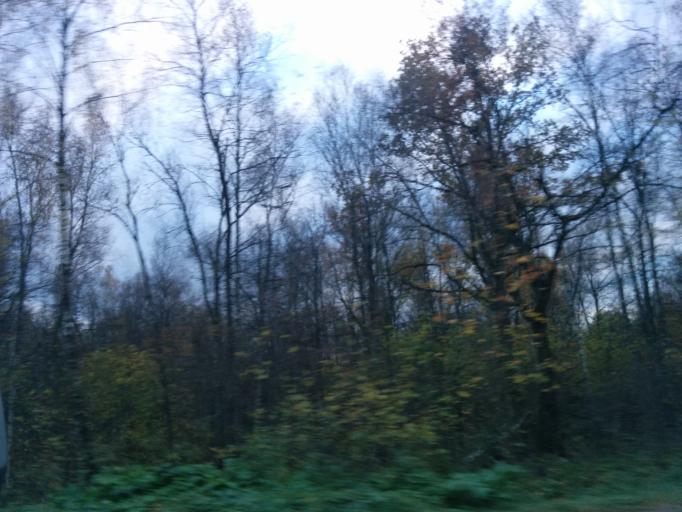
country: RU
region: Moscow
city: Annino
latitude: 55.5424
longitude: 37.6249
